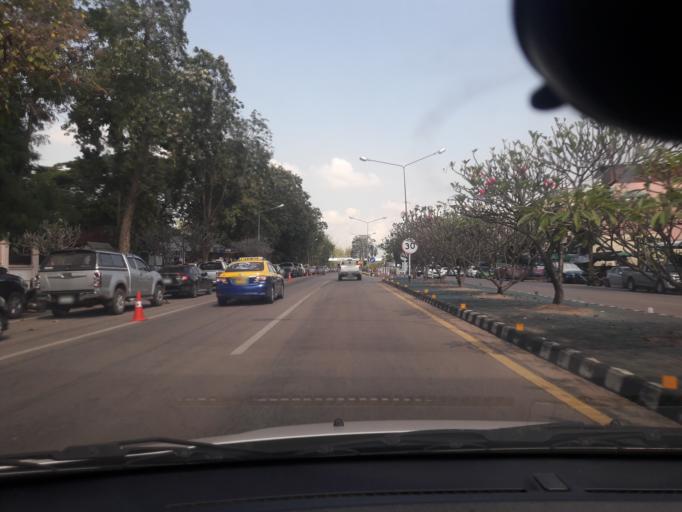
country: TH
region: Lampang
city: Lampang
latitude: 18.2330
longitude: 99.4905
